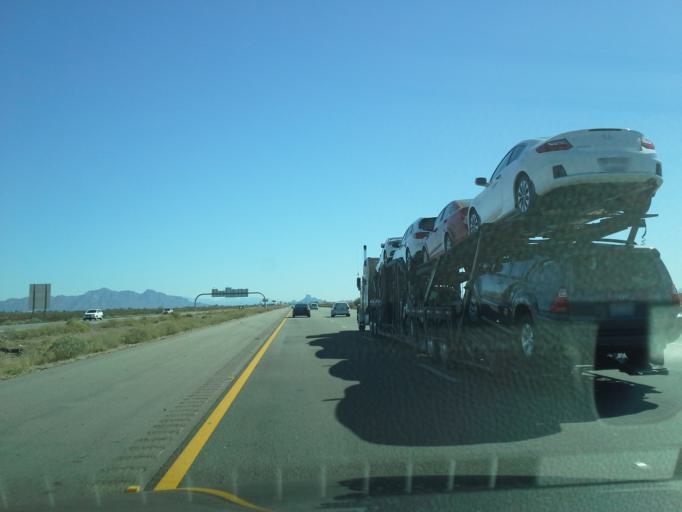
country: US
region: Arizona
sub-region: Pinal County
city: Arizona City
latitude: 32.8042
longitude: -111.6630
